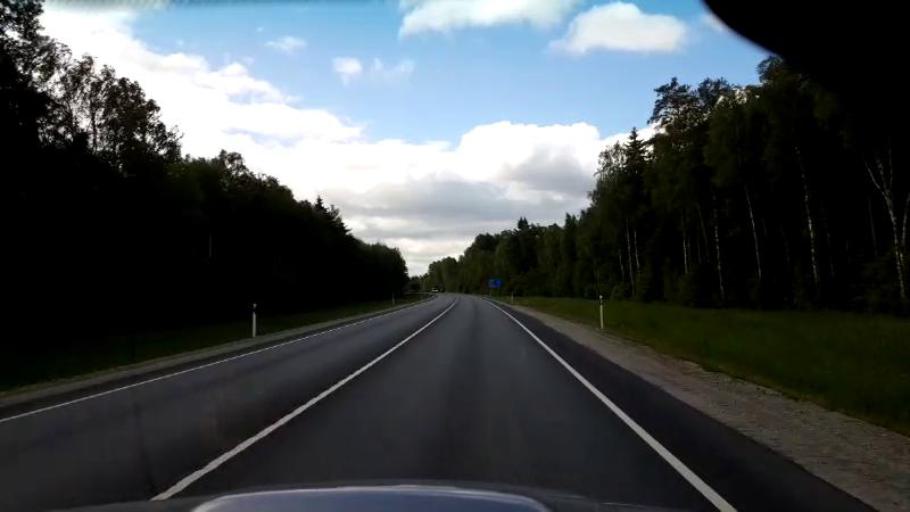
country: EE
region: Raplamaa
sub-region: Maerjamaa vald
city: Marjamaa
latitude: 59.0436
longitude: 24.4430
